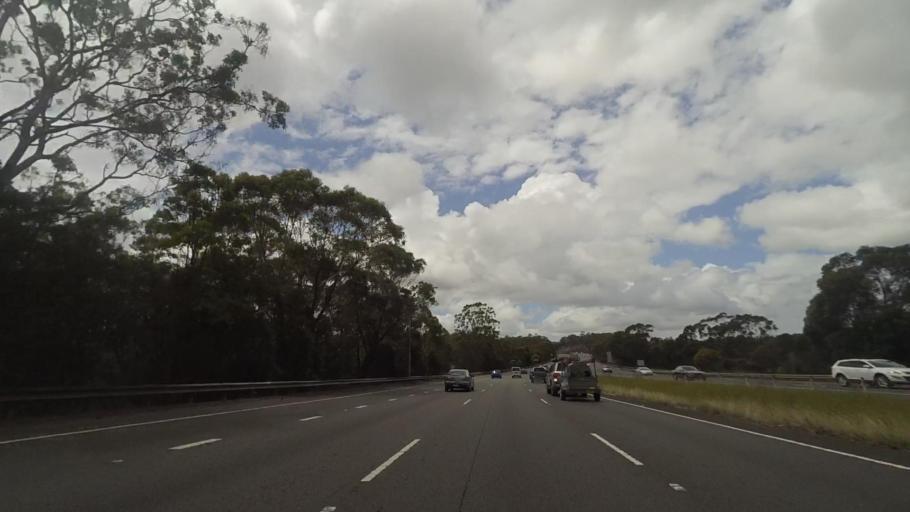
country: AU
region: New South Wales
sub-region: Gosford Shire
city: Point Clare
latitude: -33.4611
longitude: 151.1975
